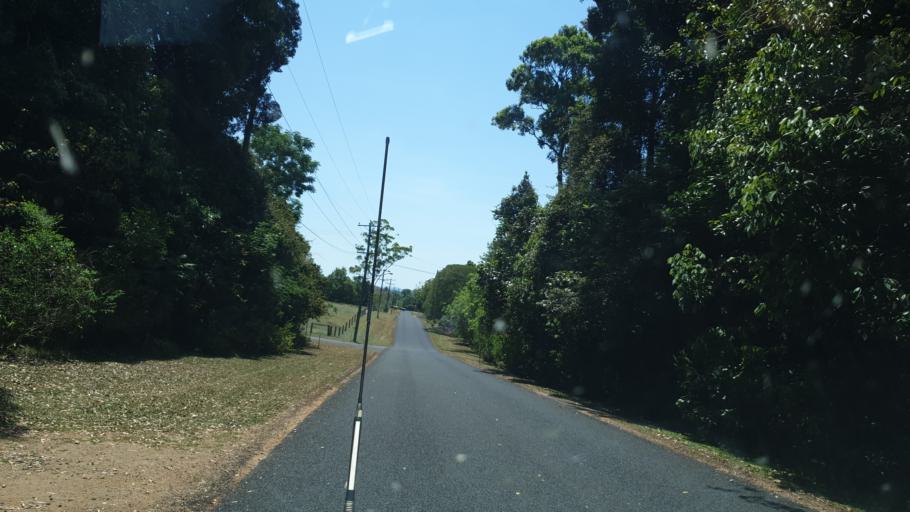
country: AU
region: Queensland
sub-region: Tablelands
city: Atherton
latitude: -17.3417
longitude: 145.6249
